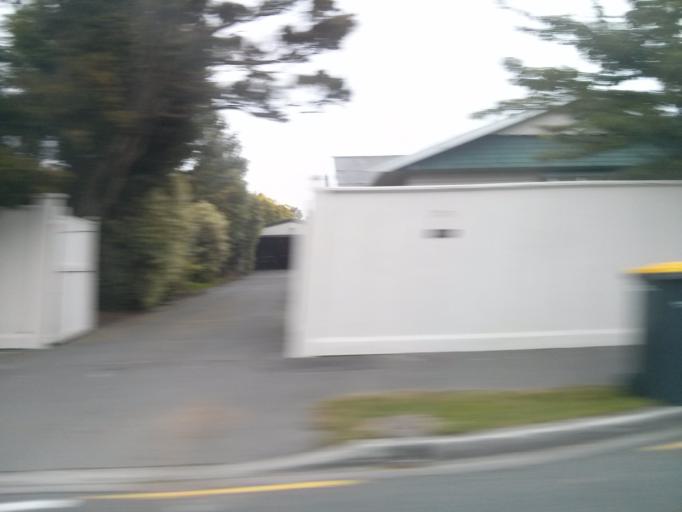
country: NZ
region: Canterbury
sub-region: Christchurch City
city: Christchurch
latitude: -43.5084
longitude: 172.6024
